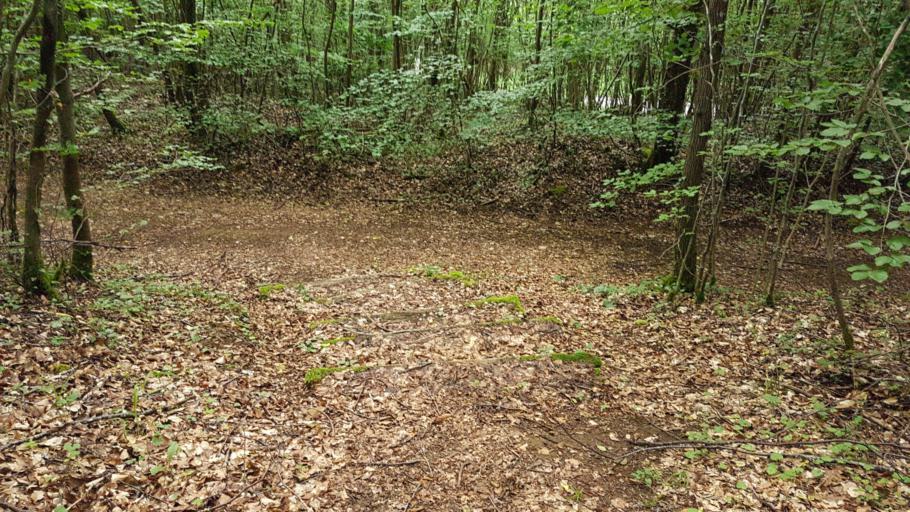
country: LU
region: Luxembourg
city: Lamadelaine
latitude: 49.5329
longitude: 5.8653
